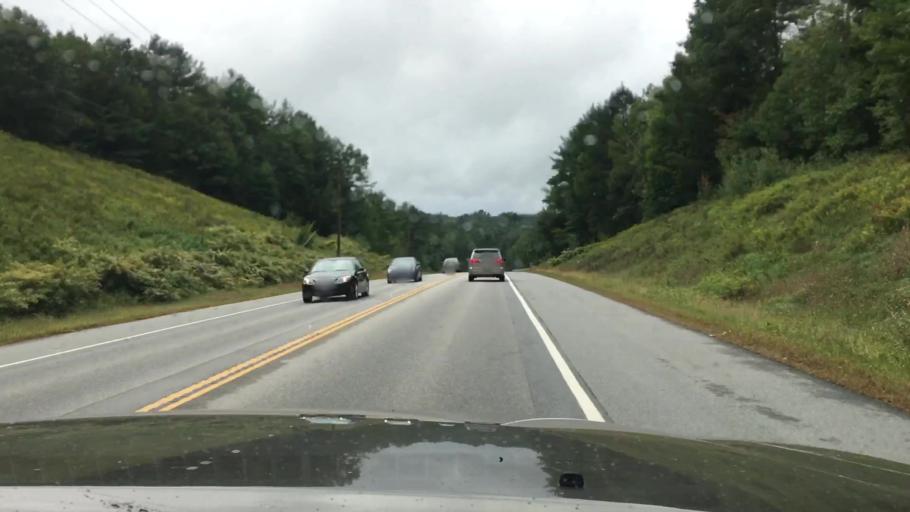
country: US
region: New Hampshire
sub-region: Cheshire County
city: Chesterfield
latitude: 42.8994
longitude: -72.4345
